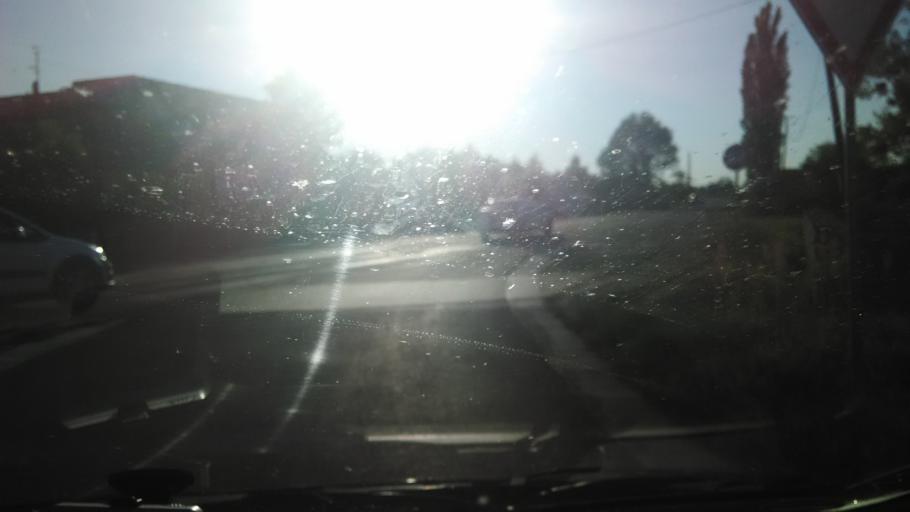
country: CZ
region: South Moravian
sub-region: Okres Breclav
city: Breclav
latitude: 48.7461
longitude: 16.9253
